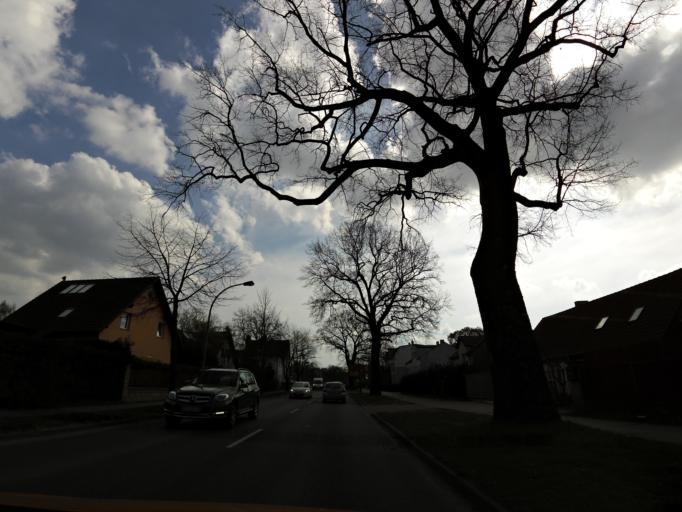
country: DE
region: Brandenburg
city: Petershagen
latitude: 52.4926
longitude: 13.7862
